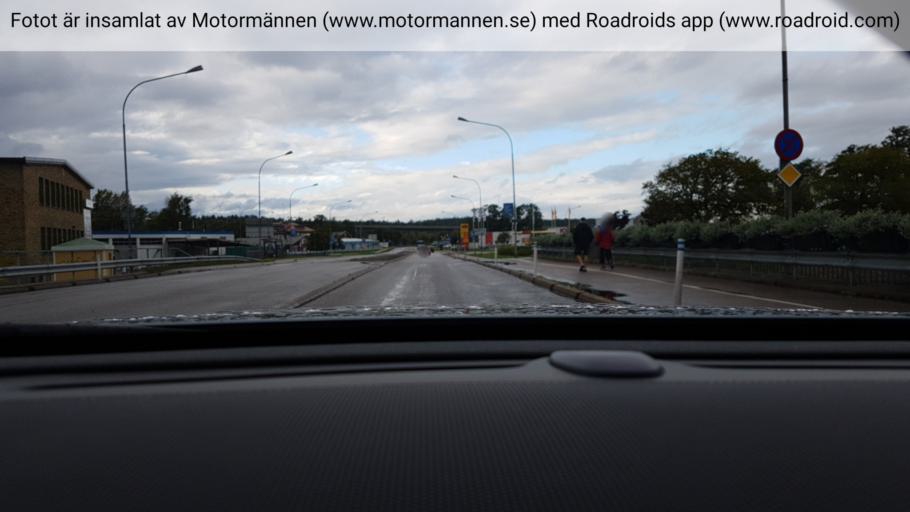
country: SE
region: Vaestra Goetaland
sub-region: Vanersborgs Kommun
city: Vanersborg
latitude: 58.3788
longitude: 12.3183
